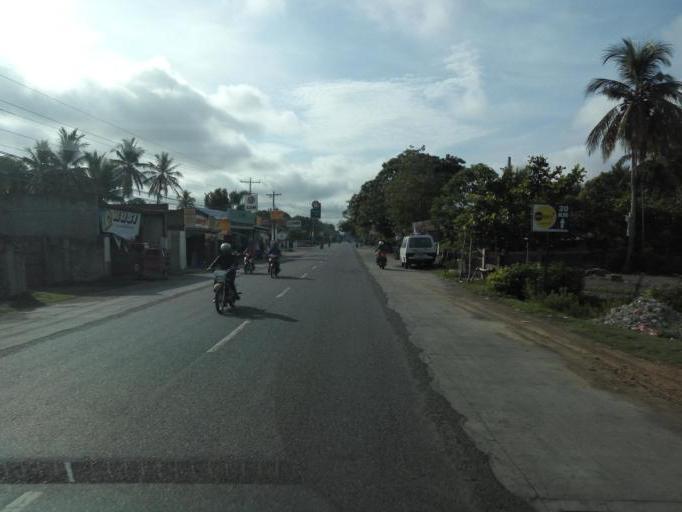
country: PH
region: Cagayan Valley
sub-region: Province of Isabela
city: Cabagan
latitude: 17.4261
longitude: 121.7751
